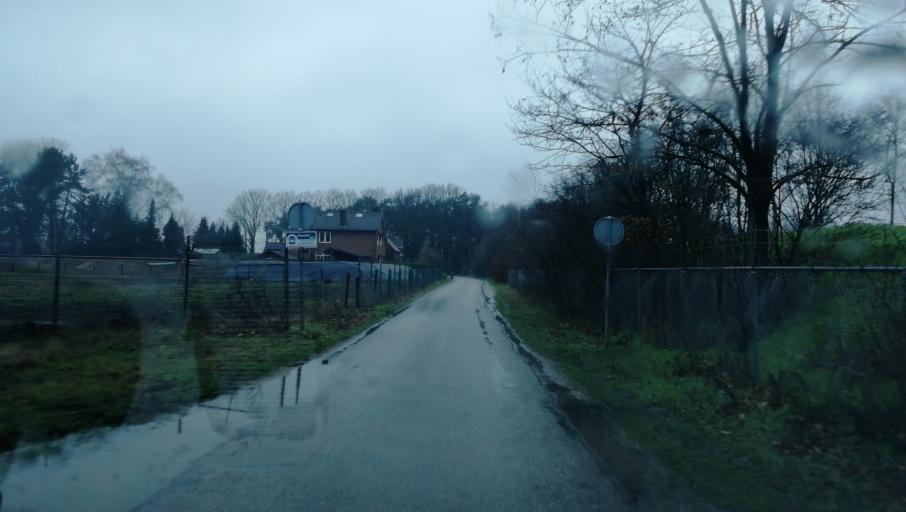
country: NL
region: Limburg
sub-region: Gemeente Venlo
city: Tegelen
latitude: 51.3476
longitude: 6.1009
